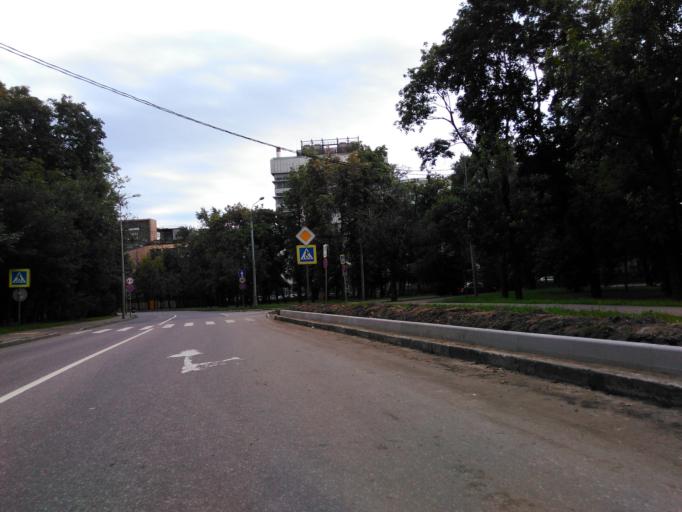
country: RU
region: Moscow
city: Taganskiy
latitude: 55.7562
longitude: 37.6699
